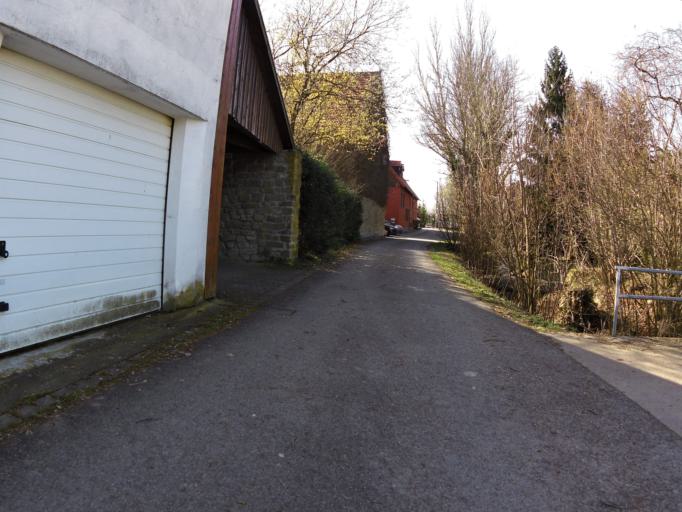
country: DE
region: Bavaria
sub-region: Regierungsbezirk Unterfranken
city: Buchbrunn
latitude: 49.7490
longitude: 10.1251
